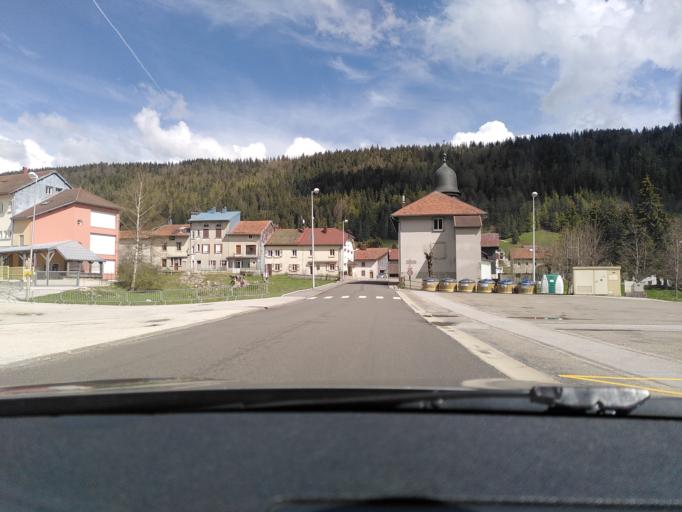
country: FR
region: Franche-Comte
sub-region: Departement du Jura
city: Les Rousses
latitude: 46.5378
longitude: 6.1370
